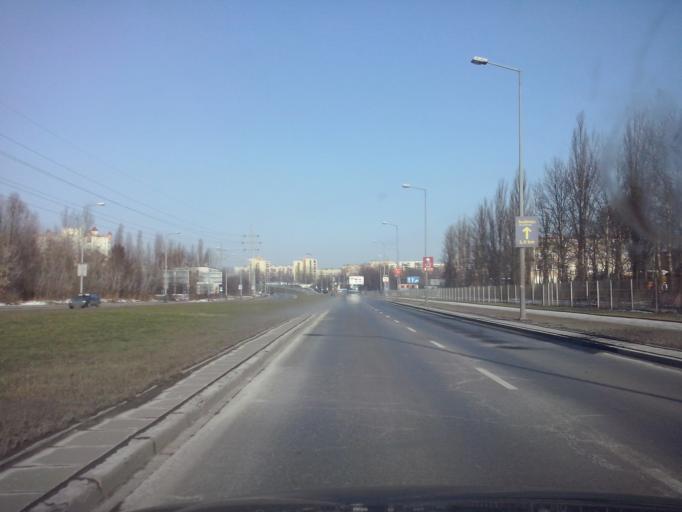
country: PL
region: Lesser Poland Voivodeship
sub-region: Krakow
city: Krakow
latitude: 50.0687
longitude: 20.0046
